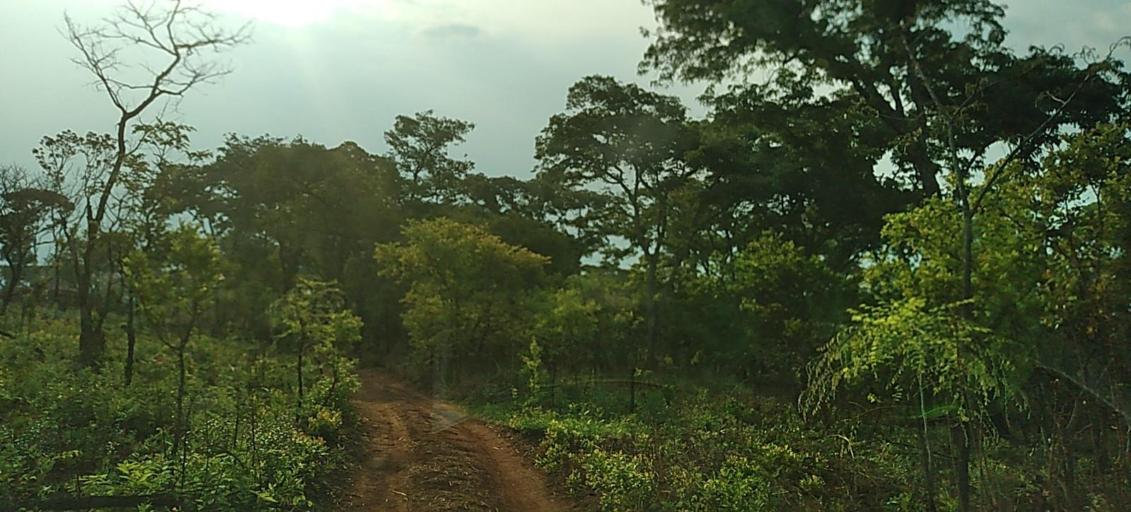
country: ZM
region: North-Western
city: Solwezi
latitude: -12.0428
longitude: 26.0481
